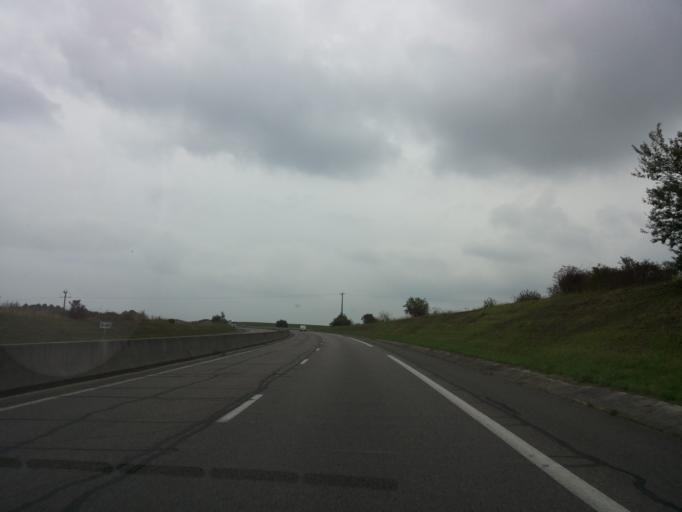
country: FR
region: Lorraine
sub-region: Departement de la Moselle
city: Sarrebourg
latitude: 48.7046
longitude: 7.0318
